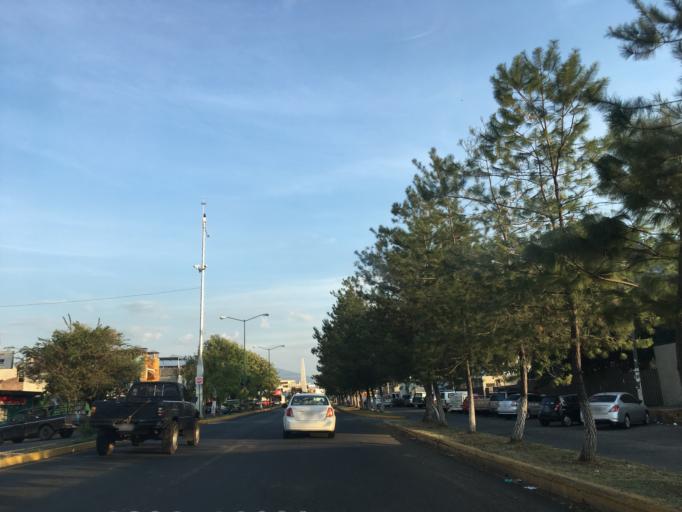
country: MX
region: Michoacan
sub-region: Los Reyes
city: La Higuerita (Colonia San Rafael)
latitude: 19.5960
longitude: -102.4735
